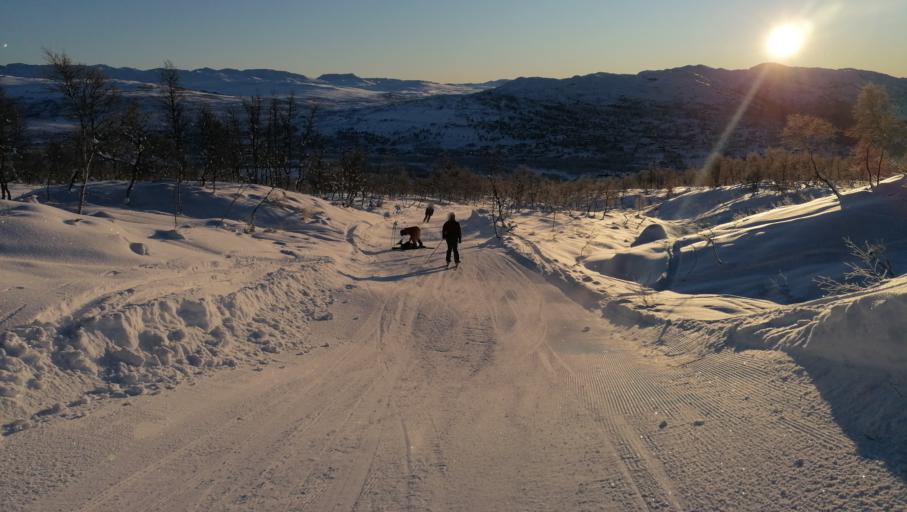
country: NO
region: Aust-Agder
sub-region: Bykle
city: Hovden
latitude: 59.5793
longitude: 7.3487
